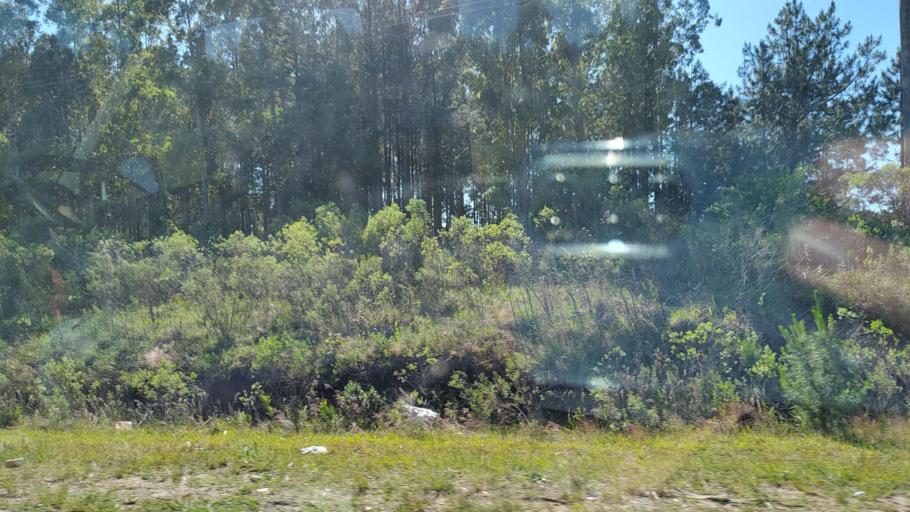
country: AR
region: Entre Rios
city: Ubajay
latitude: -31.8899
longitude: -58.3257
